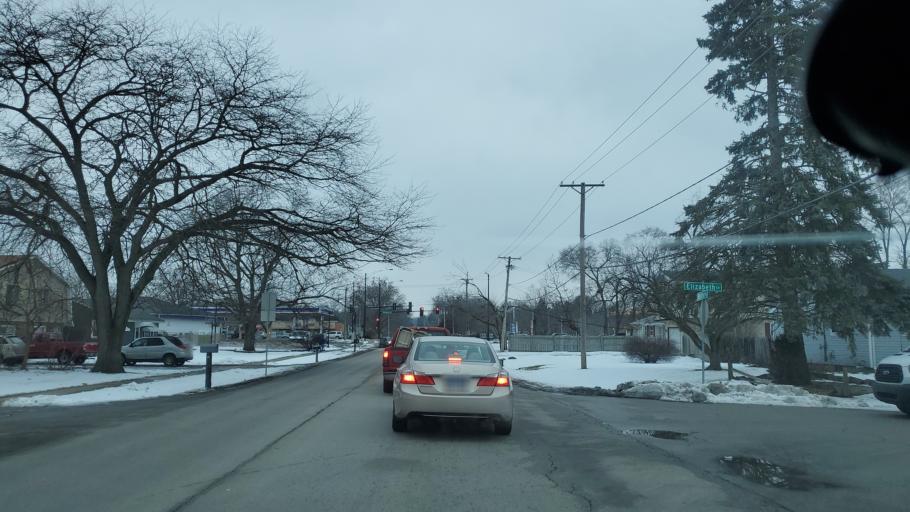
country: US
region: Illinois
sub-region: Kane County
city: North Aurora
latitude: 41.7939
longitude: -88.2802
